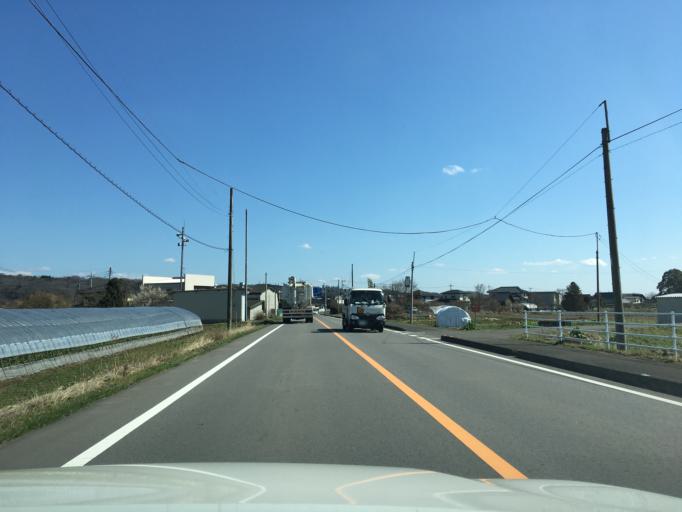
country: JP
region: Tochigi
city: Otawara
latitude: 36.7756
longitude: 140.1232
